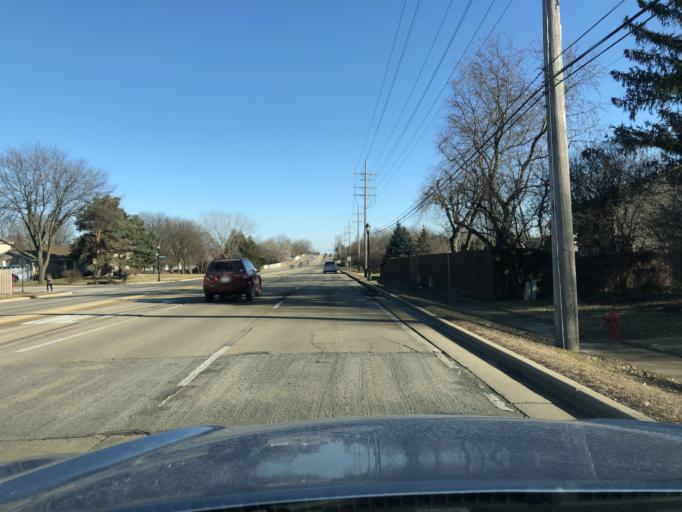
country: US
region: Illinois
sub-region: DuPage County
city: Roselle
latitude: 41.9989
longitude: -88.0536
